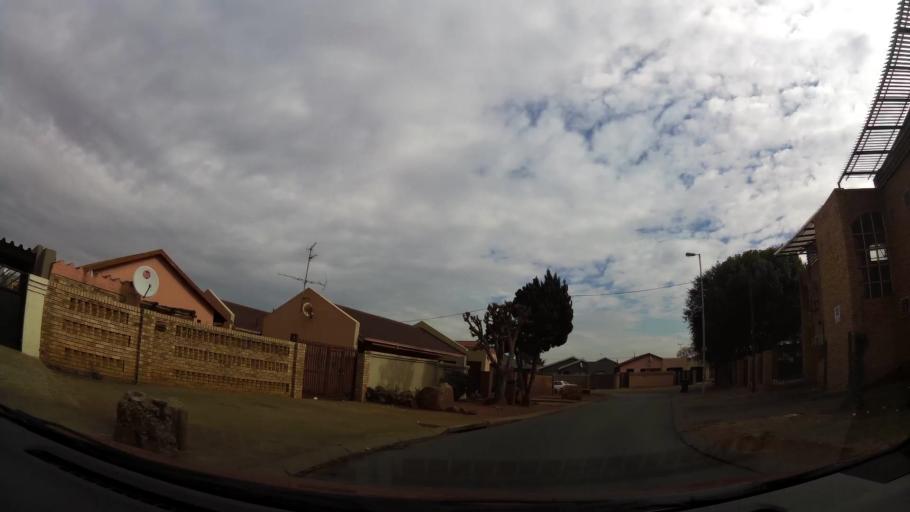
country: ZA
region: Gauteng
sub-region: City of Johannesburg Metropolitan Municipality
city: Soweto
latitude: -26.2736
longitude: 27.8311
